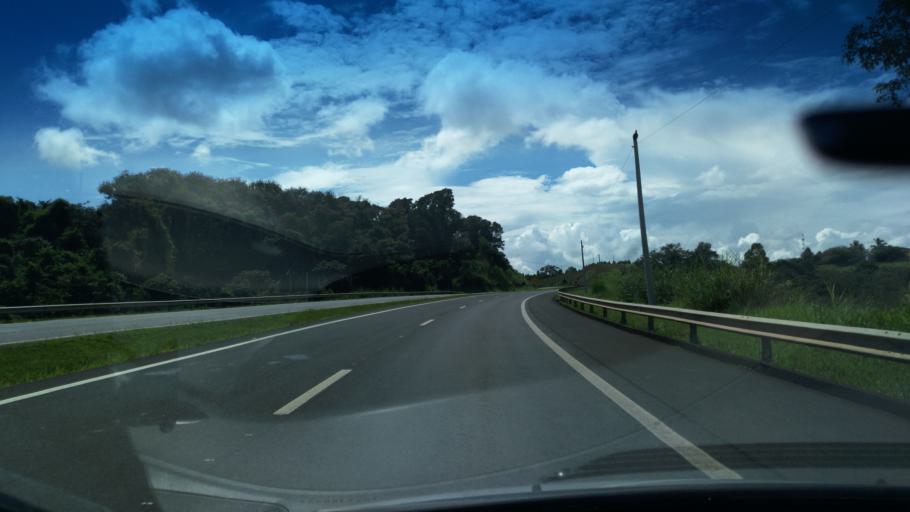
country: BR
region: Sao Paulo
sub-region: Santo Antonio Do Jardim
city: Espirito Santo do Pinhal
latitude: -22.2101
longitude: -46.7831
